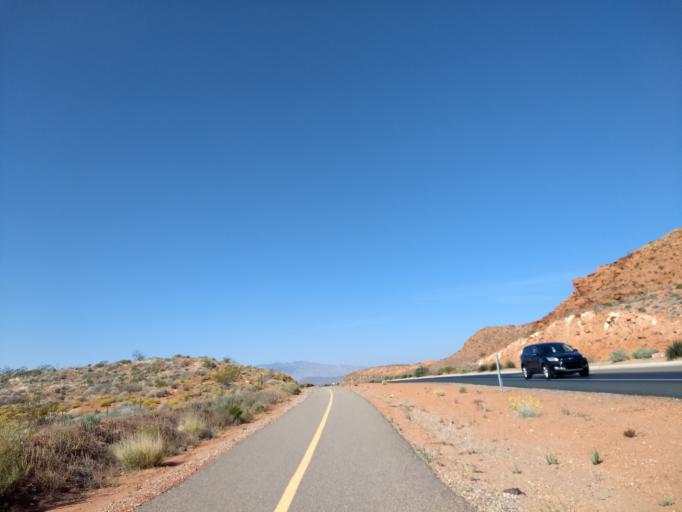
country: US
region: Utah
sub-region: Washington County
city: Saint George
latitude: 37.1334
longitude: -113.5881
